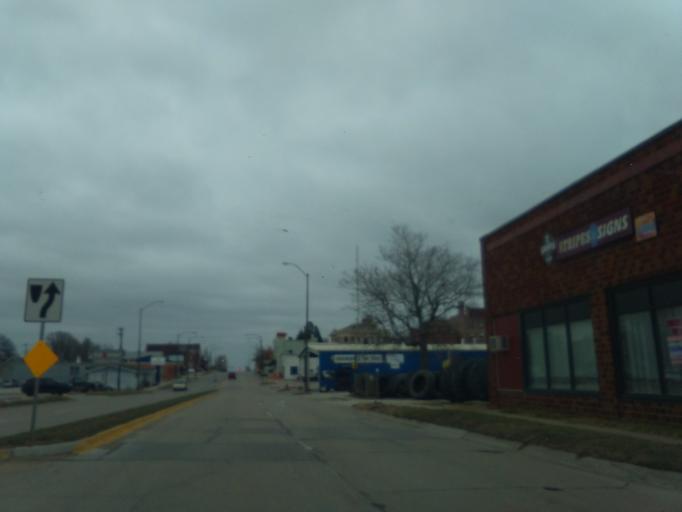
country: US
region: Nebraska
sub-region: Richardson County
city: Falls City
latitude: 40.0647
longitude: -95.6019
